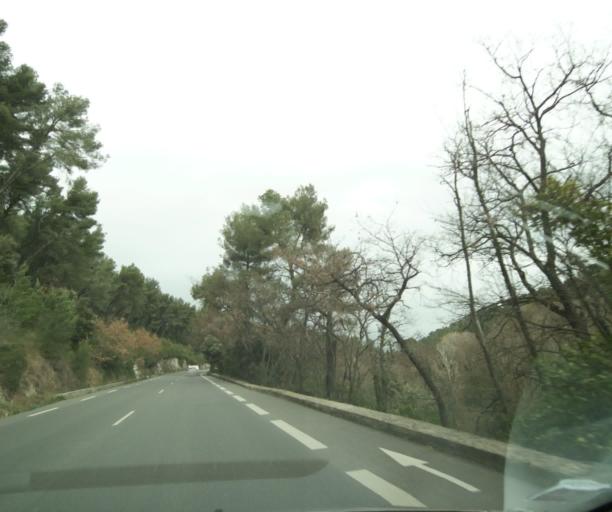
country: FR
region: Provence-Alpes-Cote d'Azur
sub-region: Departement des Bouches-du-Rhone
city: Aix-en-Provence
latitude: 43.5456
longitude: 5.4607
